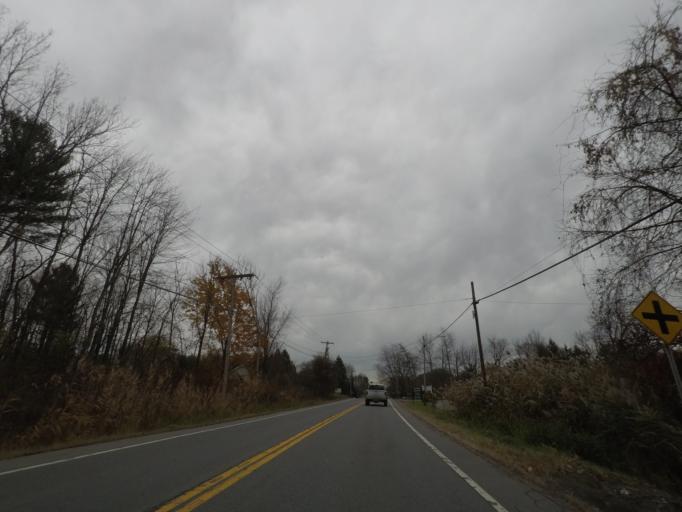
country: US
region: New York
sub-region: Albany County
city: Cohoes
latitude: 42.8226
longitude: -73.7445
